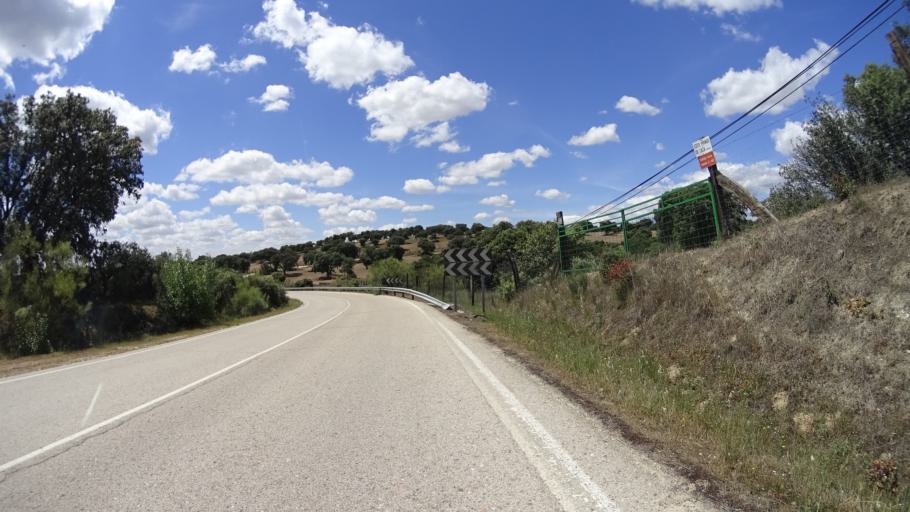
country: ES
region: Madrid
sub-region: Provincia de Madrid
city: Villanueva del Pardillo
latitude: 40.4527
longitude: -3.9532
